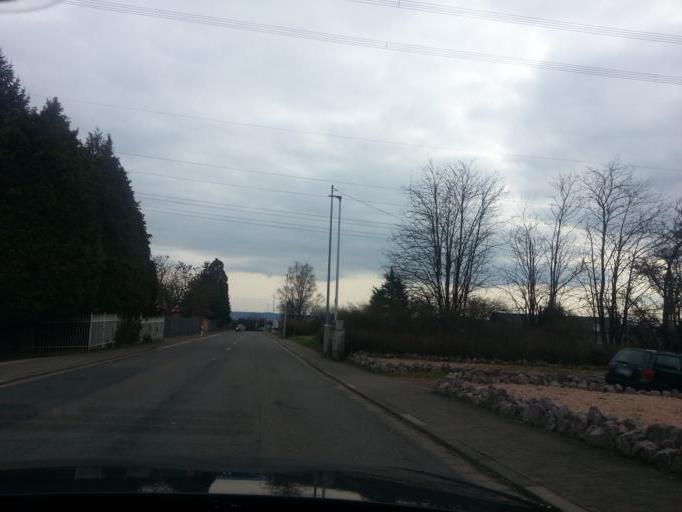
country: DE
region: Saarland
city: Bexbach
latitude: 49.3747
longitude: 7.2646
